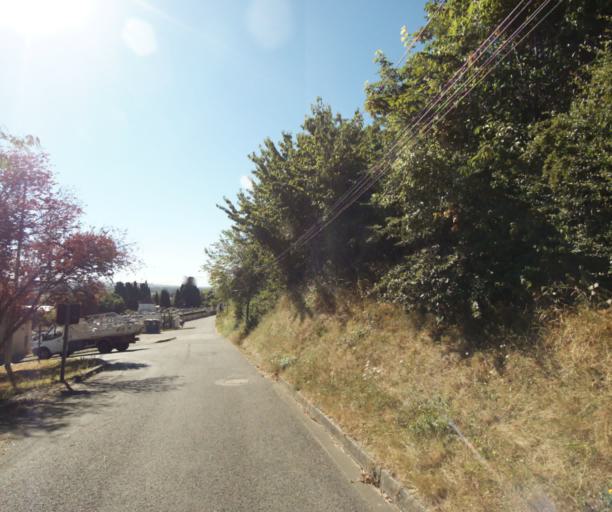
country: FR
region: Midi-Pyrenees
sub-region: Departement de la Haute-Garonne
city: Castanet-Tolosan
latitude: 43.5190
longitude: 1.4916
